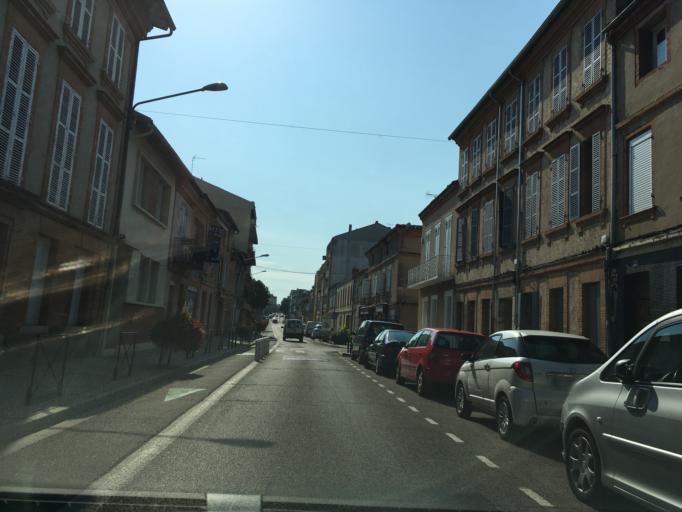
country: FR
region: Midi-Pyrenees
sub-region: Departement du Tarn-et-Garonne
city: Montauban
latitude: 44.0137
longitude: 1.3604
